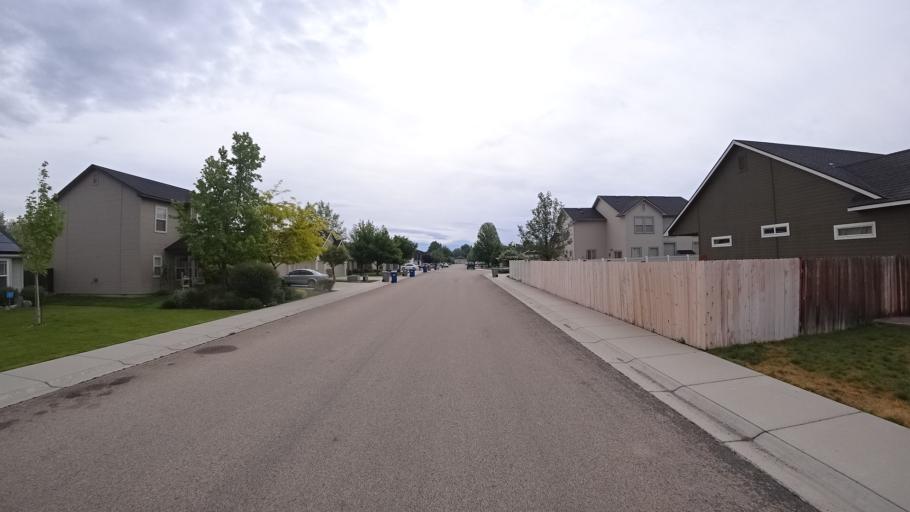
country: US
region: Idaho
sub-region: Ada County
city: Star
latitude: 43.6864
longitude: -116.4976
